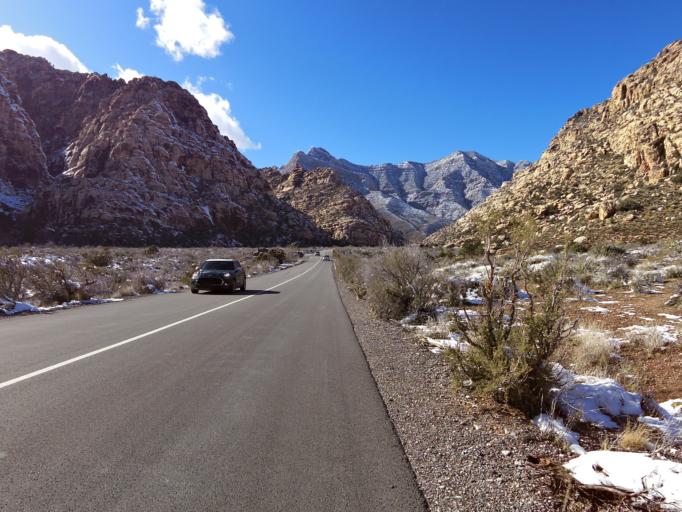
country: US
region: Nevada
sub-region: Clark County
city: Summerlin South
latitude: 36.1569
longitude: -115.4918
